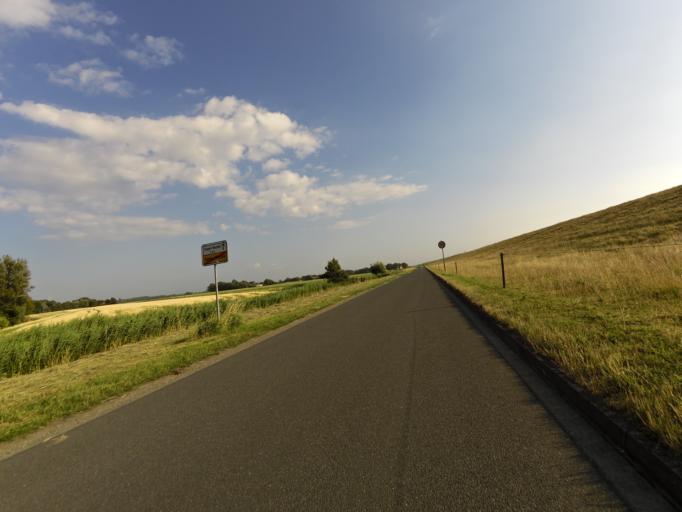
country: DE
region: Lower Saxony
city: Nordholz
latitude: 53.7838
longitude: 8.5509
